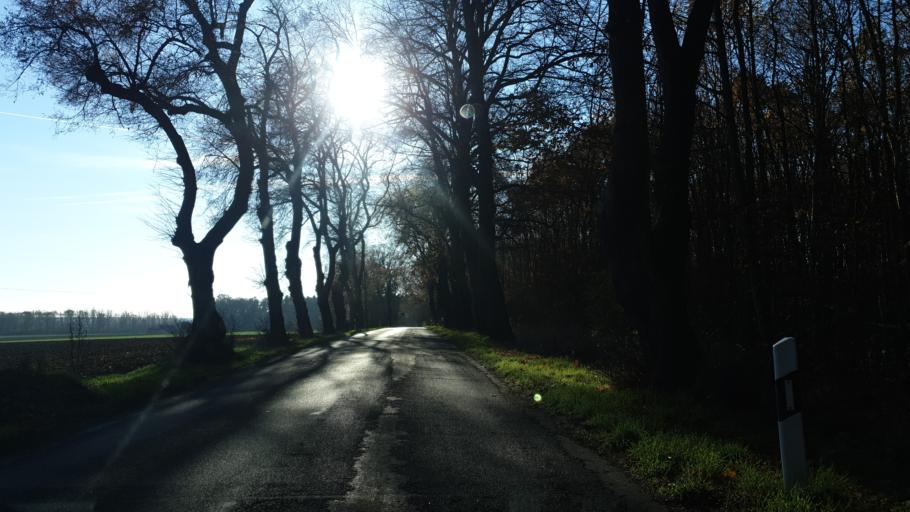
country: DE
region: Saxony-Anhalt
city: Droyssig
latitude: 51.0290
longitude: 12.0210
